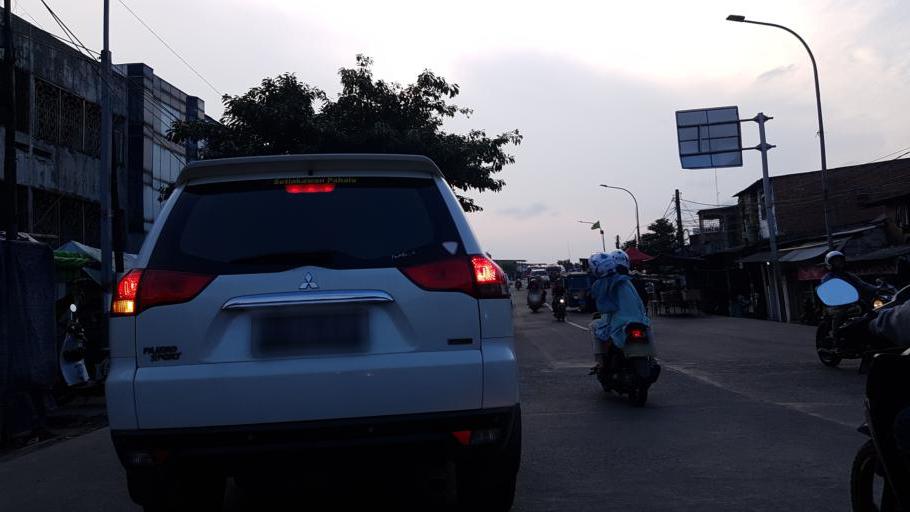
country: ID
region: Jakarta Raya
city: Jakarta
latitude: -6.1387
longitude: 106.7772
